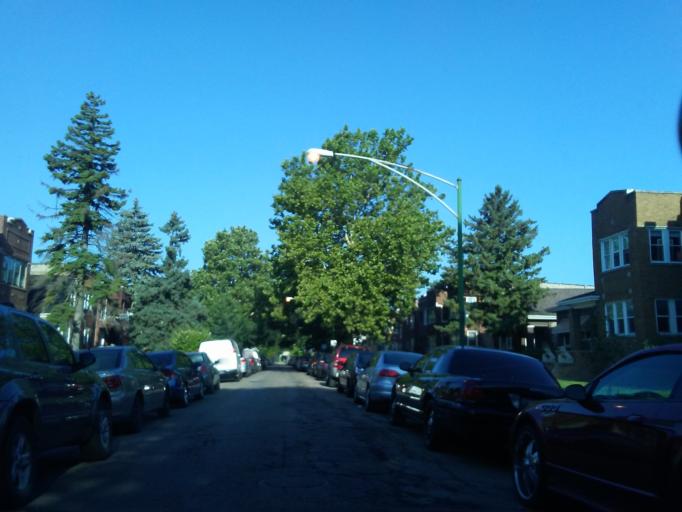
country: US
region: Illinois
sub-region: Cook County
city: Lincolnwood
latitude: 41.9354
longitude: -87.7303
